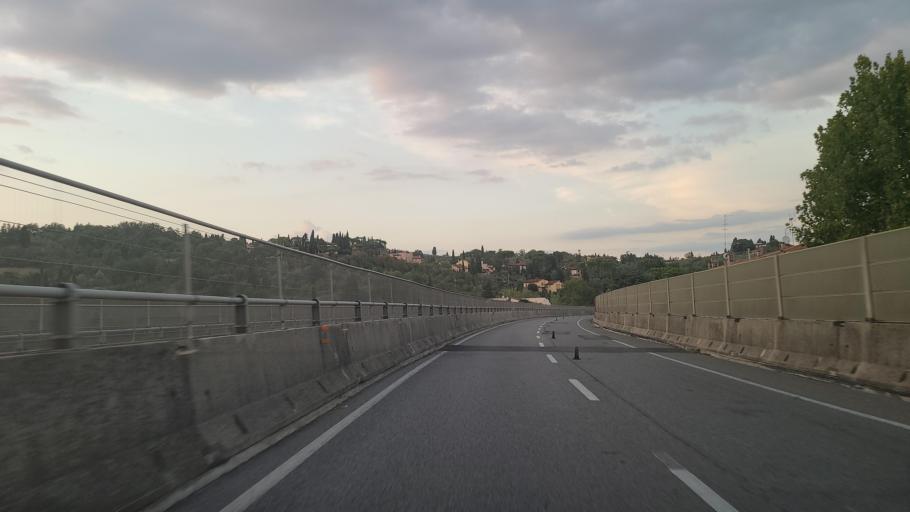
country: IT
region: Tuscany
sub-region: Province of Florence
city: Tavarnuzze
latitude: 43.7079
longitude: 11.2131
